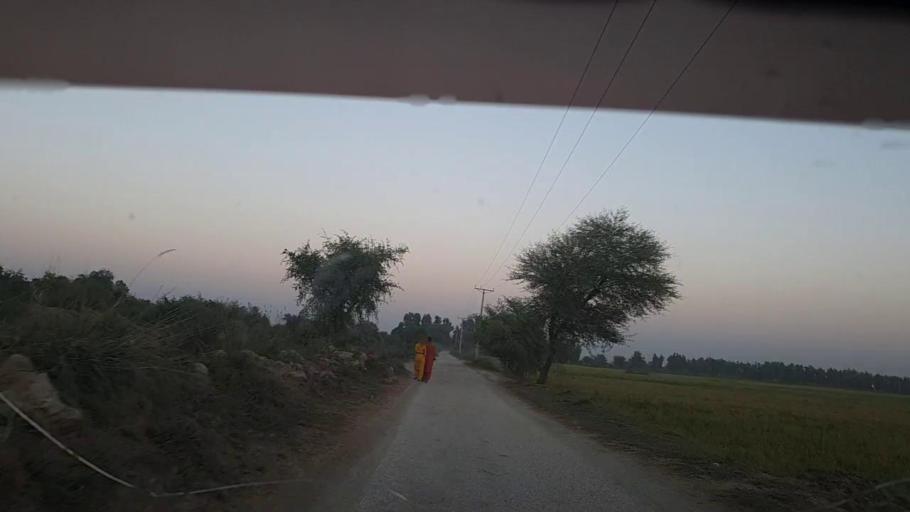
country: PK
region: Sindh
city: Ratodero
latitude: 27.8638
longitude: 68.2648
